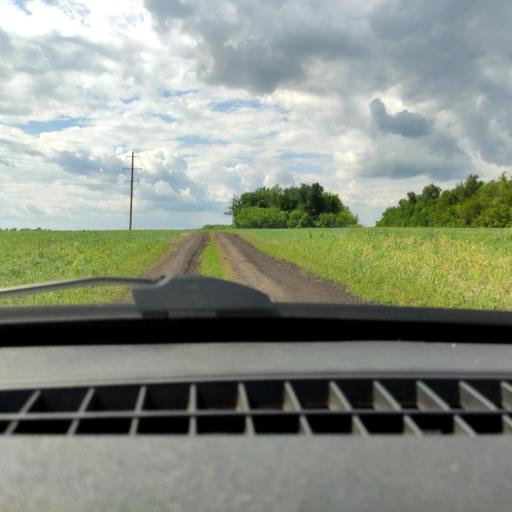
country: RU
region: Bashkortostan
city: Kabakovo
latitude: 54.5139
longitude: 56.0990
